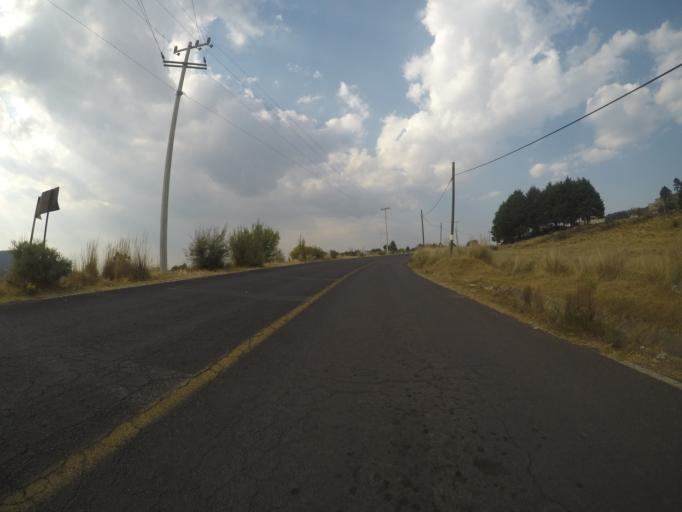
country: MX
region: Mexico
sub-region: Xalatlaco
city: El Aguila (La Mesa)
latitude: 19.1600
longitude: -99.3967
